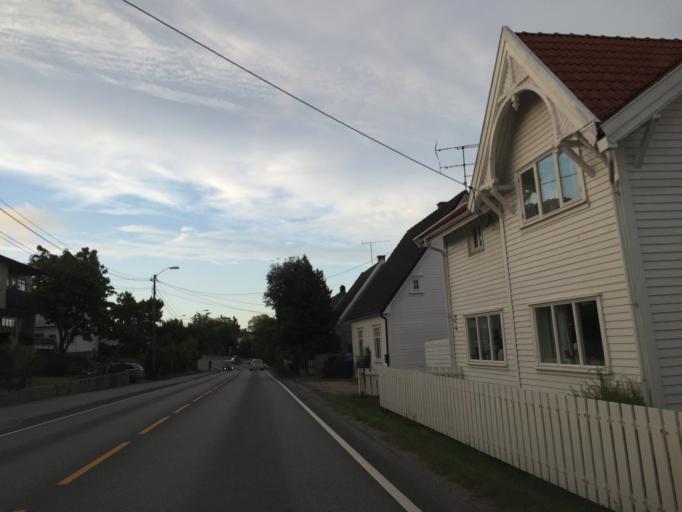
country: NO
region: Ostfold
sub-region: Fredrikstad
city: Fredrikstad
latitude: 59.1959
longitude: 10.9419
